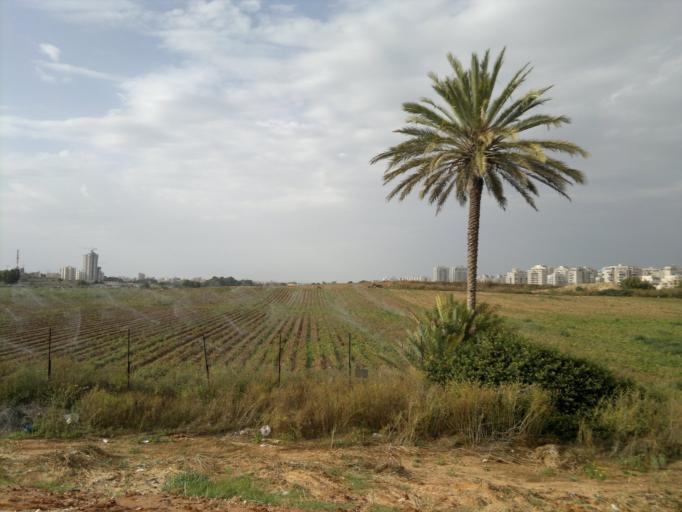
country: IL
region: Central District
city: Even Yehuda
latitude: 32.2955
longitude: 34.8649
